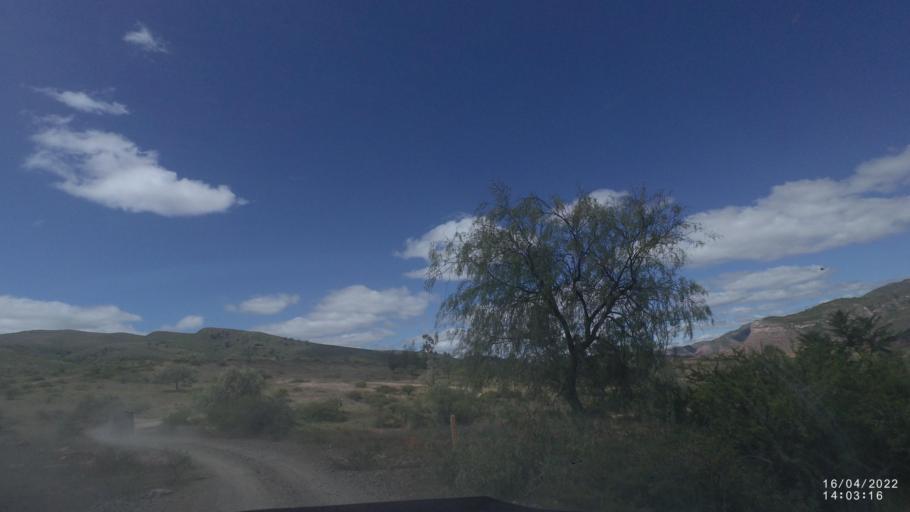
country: BO
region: Cochabamba
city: Mizque
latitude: -18.0498
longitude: -65.5425
